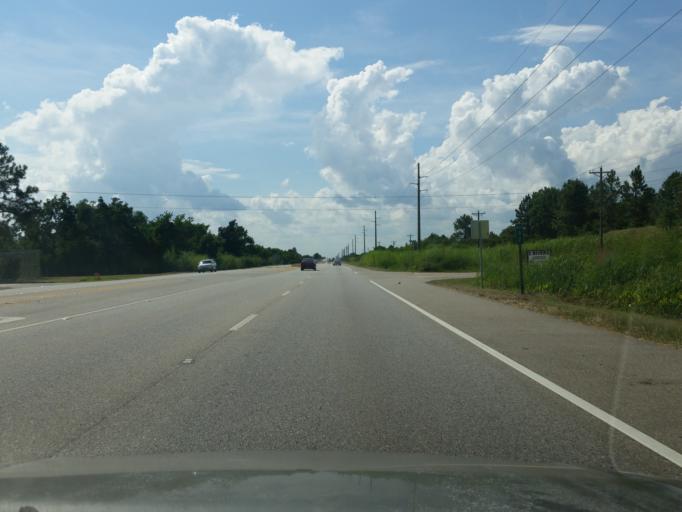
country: US
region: Alabama
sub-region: Baldwin County
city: Spanish Fort
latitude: 30.6698
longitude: -87.9352
